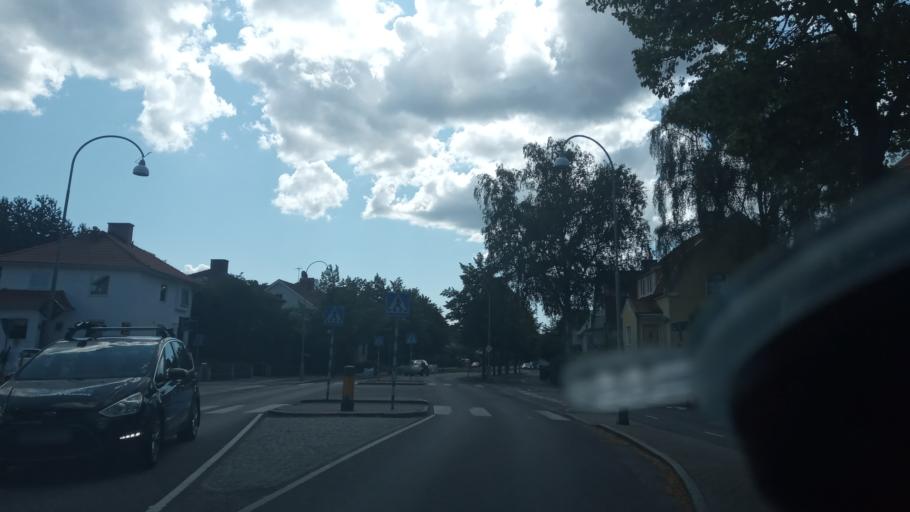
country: SE
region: Vaestra Goetaland
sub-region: Goteborg
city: Goeteborg
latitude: 57.6943
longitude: 12.0027
